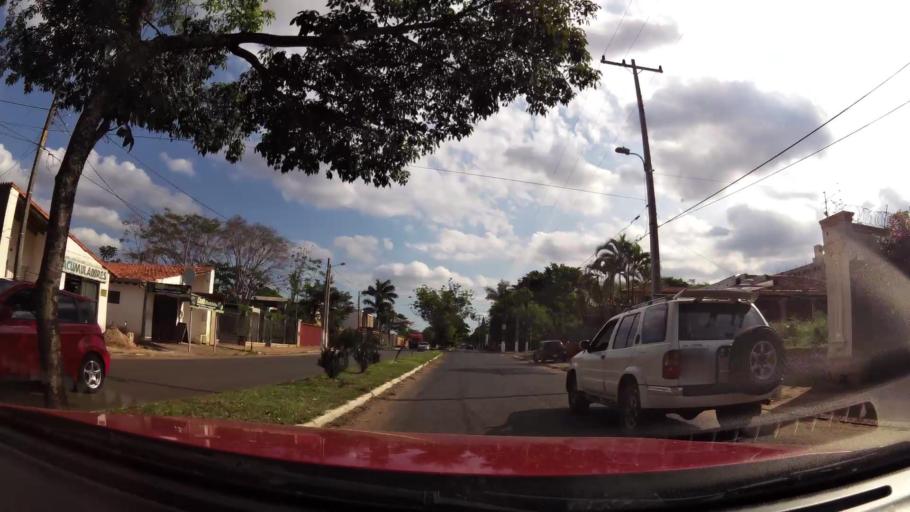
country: PY
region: Central
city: Fernando de la Mora
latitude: -25.3422
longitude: -57.5405
